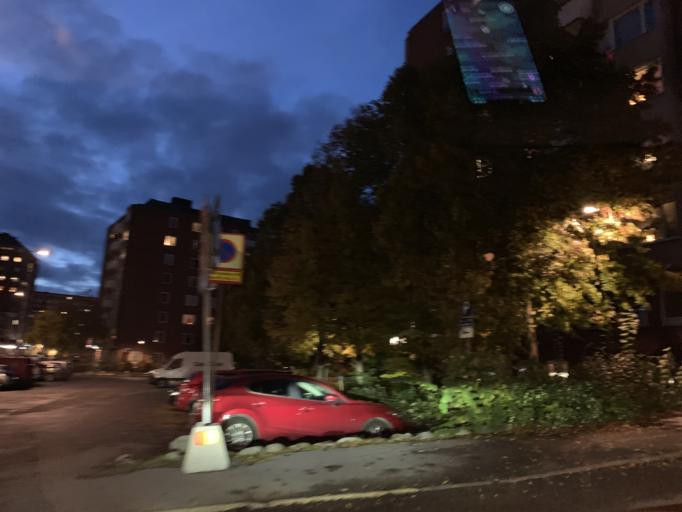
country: SE
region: Stockholm
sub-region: Huddinge Kommun
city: Huddinge
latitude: 59.2347
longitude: 17.9857
